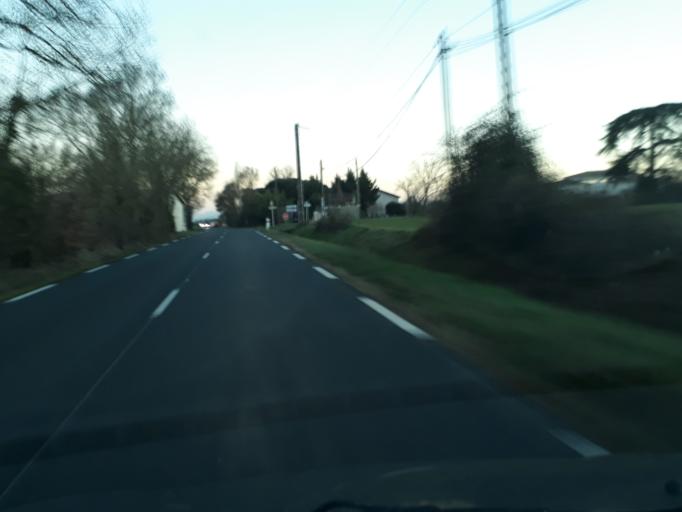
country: FR
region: Midi-Pyrenees
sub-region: Departement de la Haute-Garonne
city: Saint-Lys
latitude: 43.5391
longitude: 1.1634
